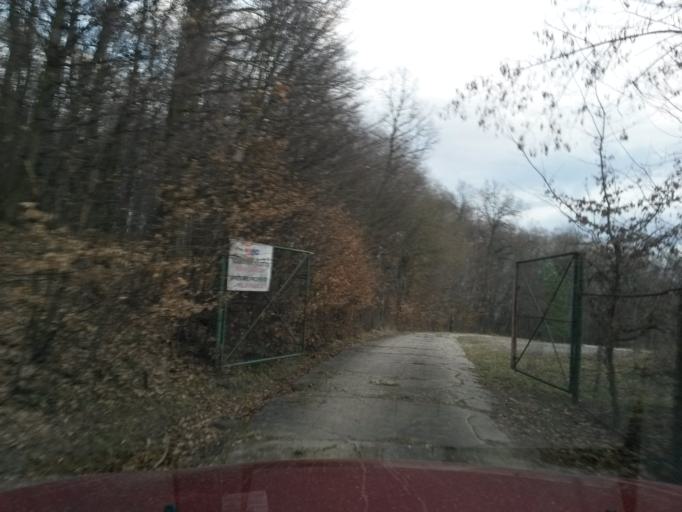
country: SK
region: Kosicky
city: Kosice
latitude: 48.6920
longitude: 21.3082
